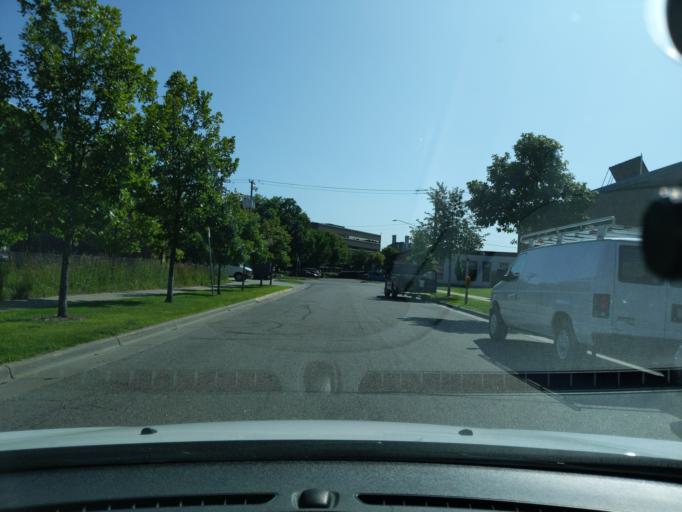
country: US
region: Minnesota
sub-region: Ramsey County
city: Lauderdale
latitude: 44.9748
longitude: -93.2266
